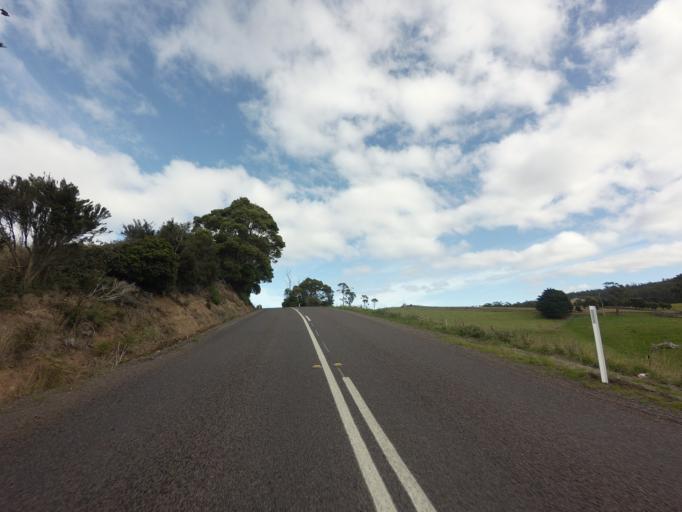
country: AU
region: Tasmania
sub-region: Clarence
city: Sandford
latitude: -43.0659
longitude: 147.7473
